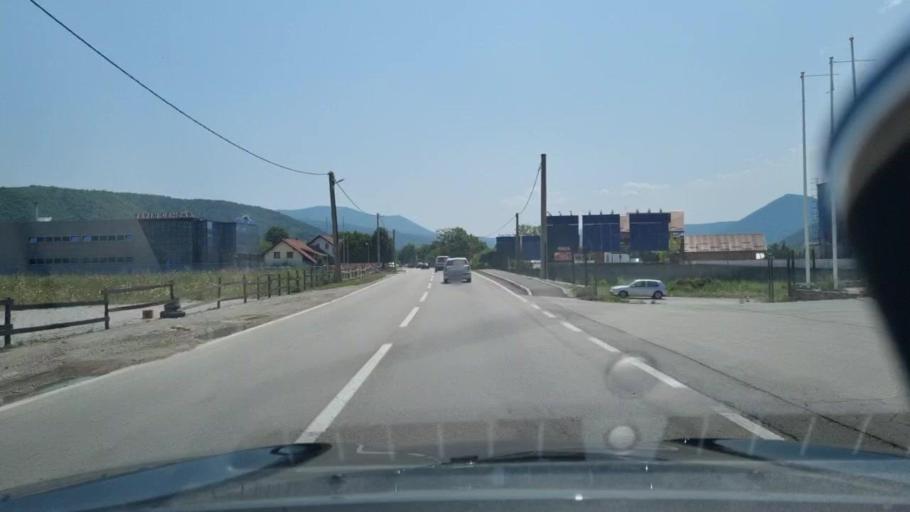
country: BA
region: Federation of Bosnia and Herzegovina
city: Bihac
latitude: 44.7961
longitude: 15.9196
